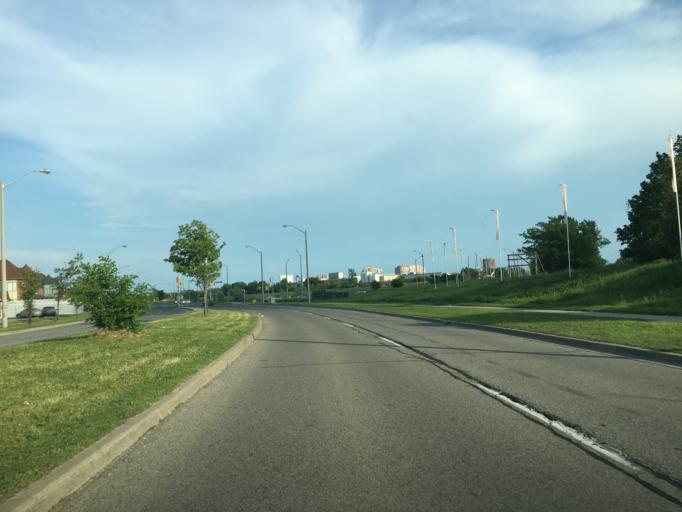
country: CA
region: Ontario
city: Markham
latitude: 43.8239
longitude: -79.2314
